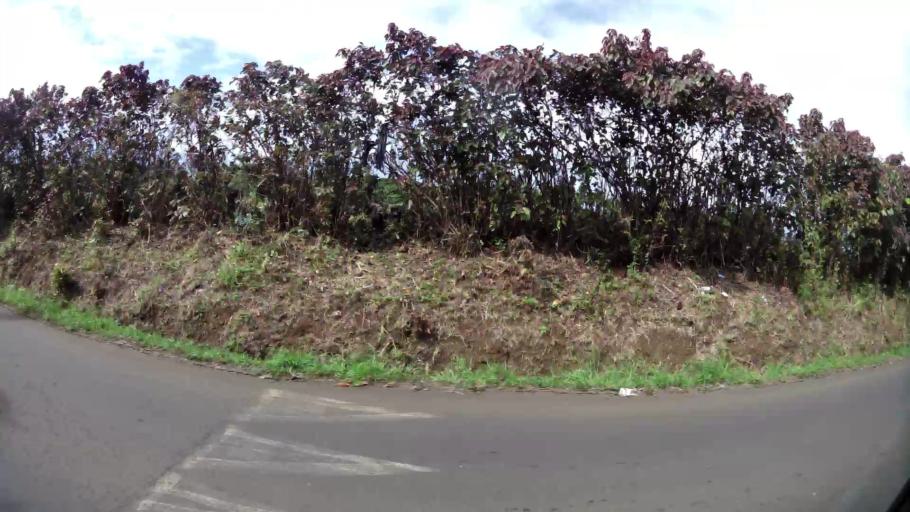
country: RE
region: Reunion
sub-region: Reunion
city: Sainte-Marie
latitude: -20.9006
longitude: 55.5698
